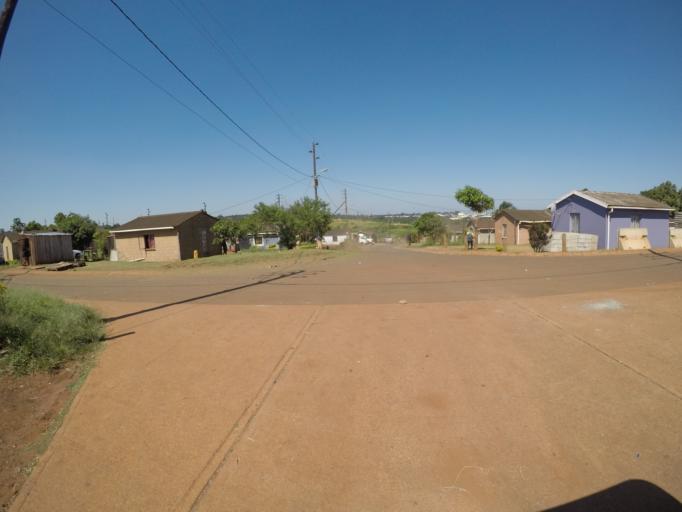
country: ZA
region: KwaZulu-Natal
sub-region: uThungulu District Municipality
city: Empangeni
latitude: -28.7698
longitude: 31.8781
